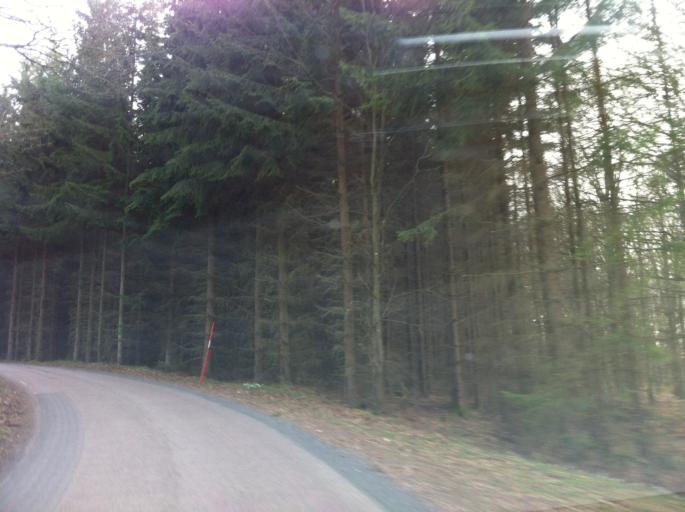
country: SE
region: Skane
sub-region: Eslovs Kommun
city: Stehag
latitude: 56.0113
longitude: 13.3942
